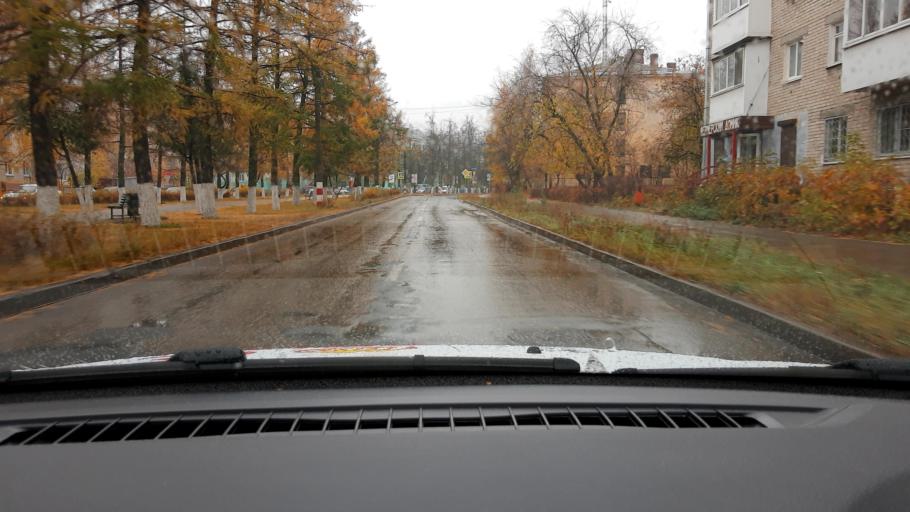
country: RU
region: Nizjnij Novgorod
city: Dzerzhinsk
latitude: 56.2384
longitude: 43.4433
